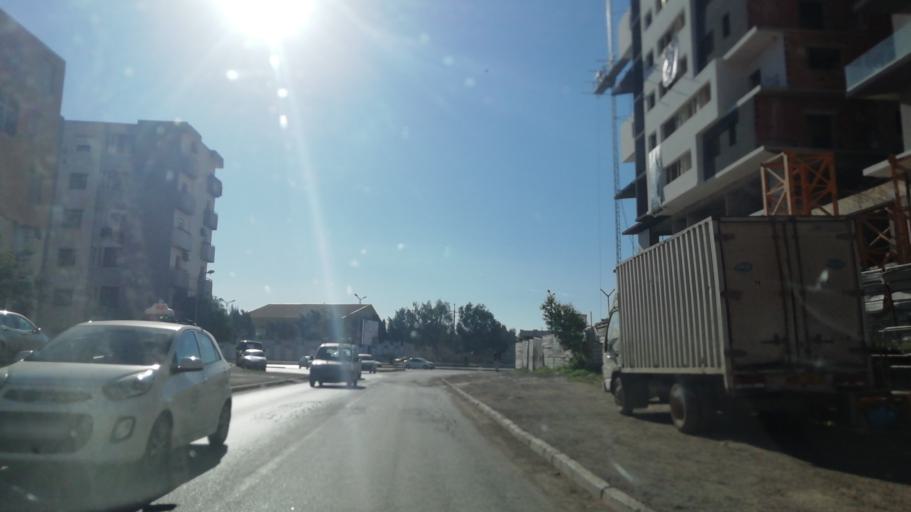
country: DZ
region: Oran
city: Oran
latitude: 35.6668
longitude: -0.6468
